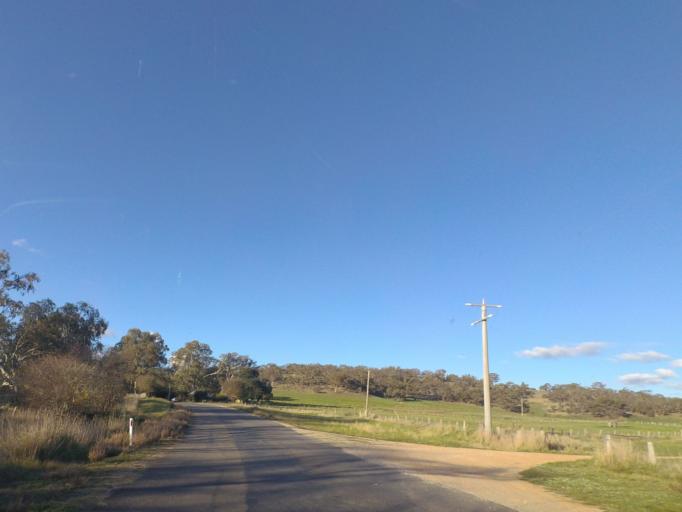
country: AU
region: Victoria
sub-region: Mount Alexander
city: Castlemaine
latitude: -37.1474
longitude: 144.1844
